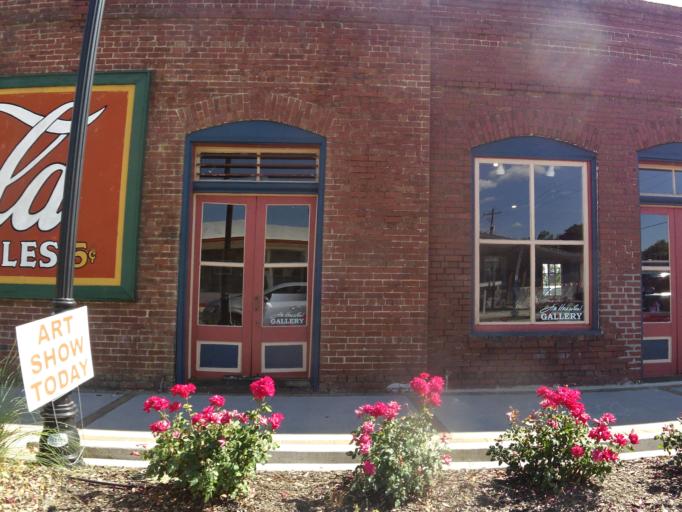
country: US
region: South Carolina
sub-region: Bamberg County
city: Denmark
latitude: 33.3261
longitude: -81.1424
